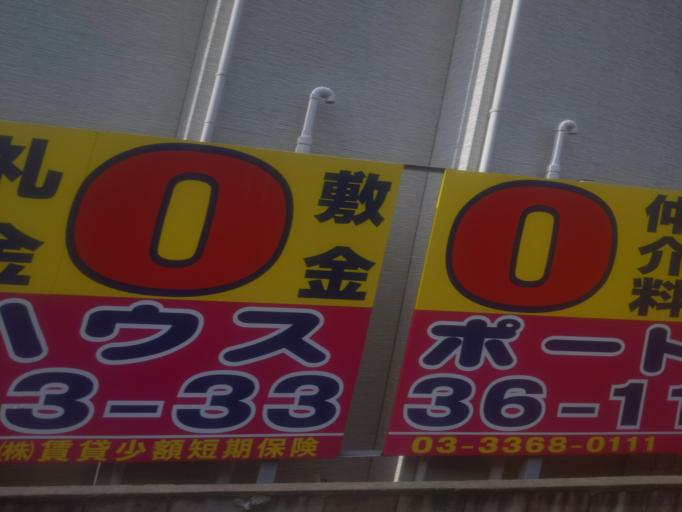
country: JP
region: Tokyo
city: Tokyo
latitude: 35.7216
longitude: 139.6471
